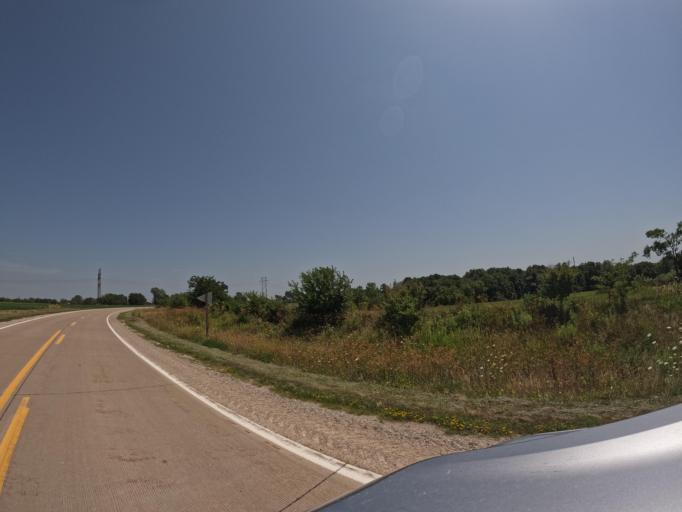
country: US
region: Iowa
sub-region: Henry County
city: Mount Pleasant
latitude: 40.9851
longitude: -91.6331
